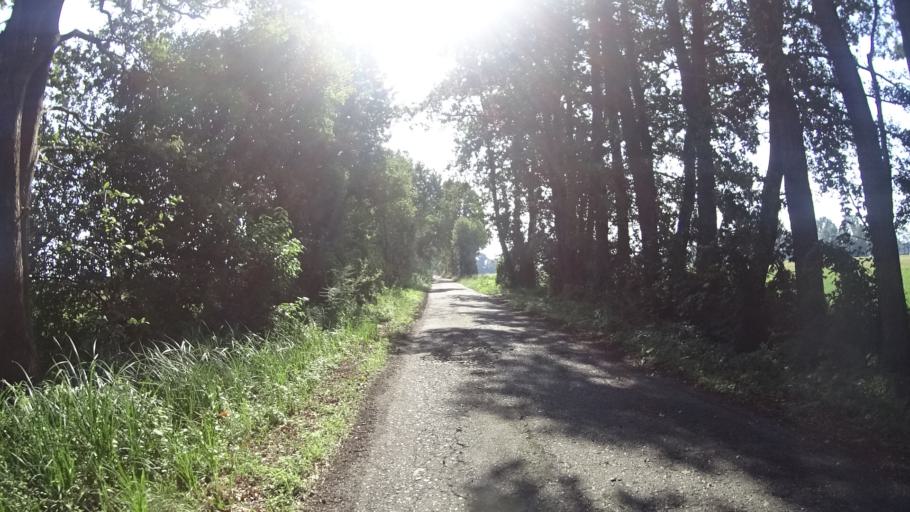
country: DE
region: Brandenburg
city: Neu Zauche
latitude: 51.9115
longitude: 14.0536
